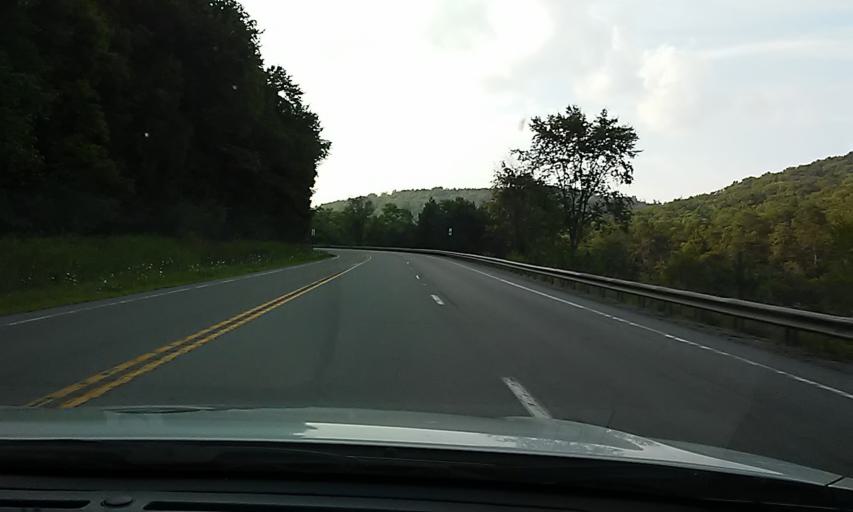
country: US
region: Pennsylvania
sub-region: McKean County
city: Smethport
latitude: 41.7083
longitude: -78.5946
